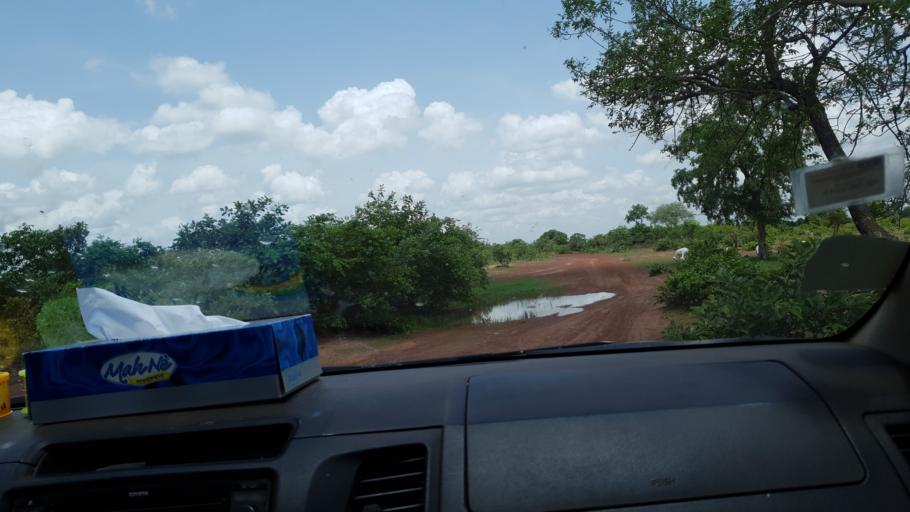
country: ML
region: Koulikoro
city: Banamba
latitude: 13.3783
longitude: -7.2141
